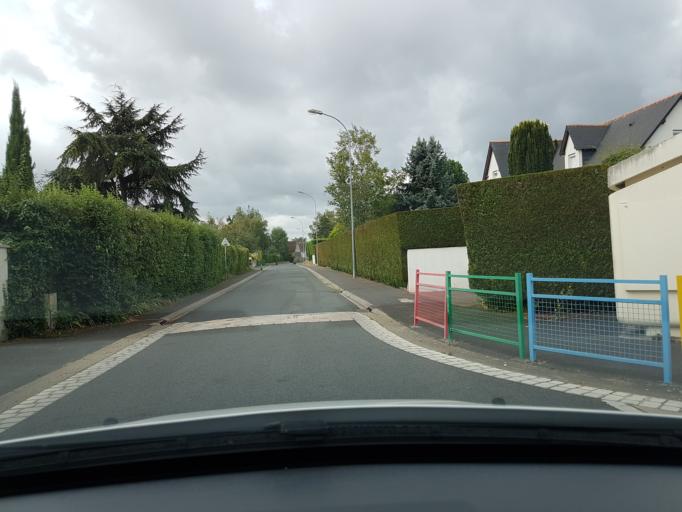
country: FR
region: Centre
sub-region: Departement d'Indre-et-Loire
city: Larcay
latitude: 47.3570
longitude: 0.7724
